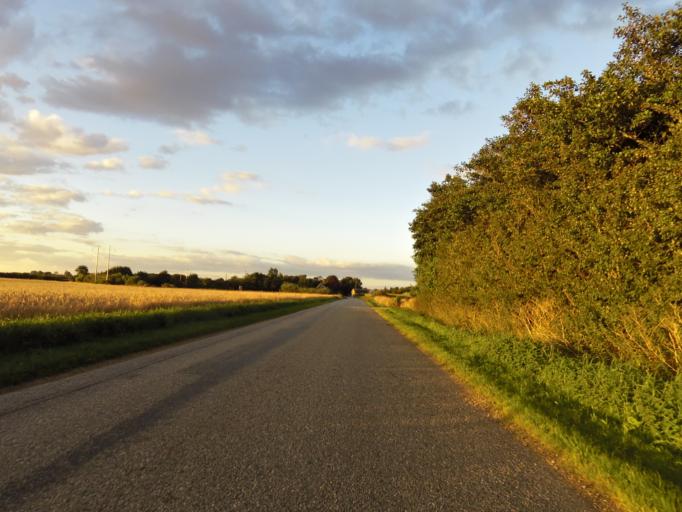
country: DK
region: South Denmark
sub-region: Esbjerg Kommune
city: Ribe
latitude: 55.2458
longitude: 8.8937
